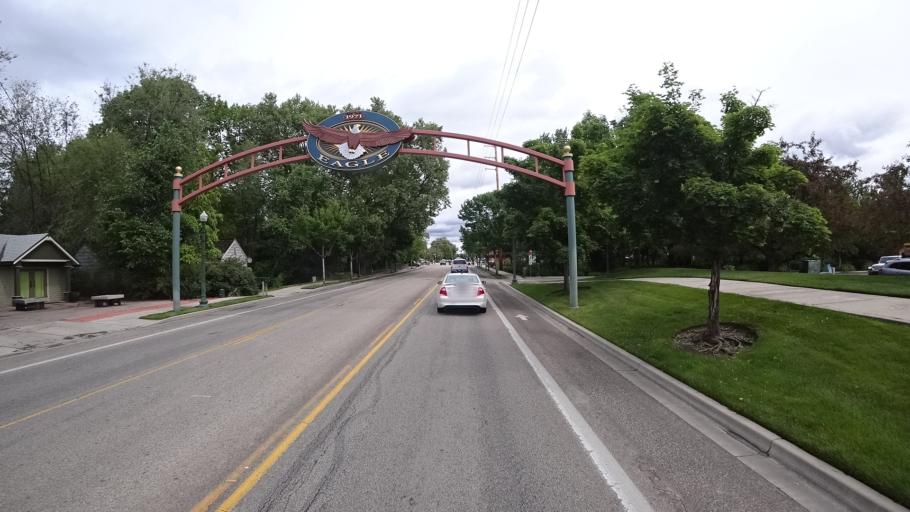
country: US
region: Idaho
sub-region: Ada County
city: Eagle
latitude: 43.6933
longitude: -116.3540
